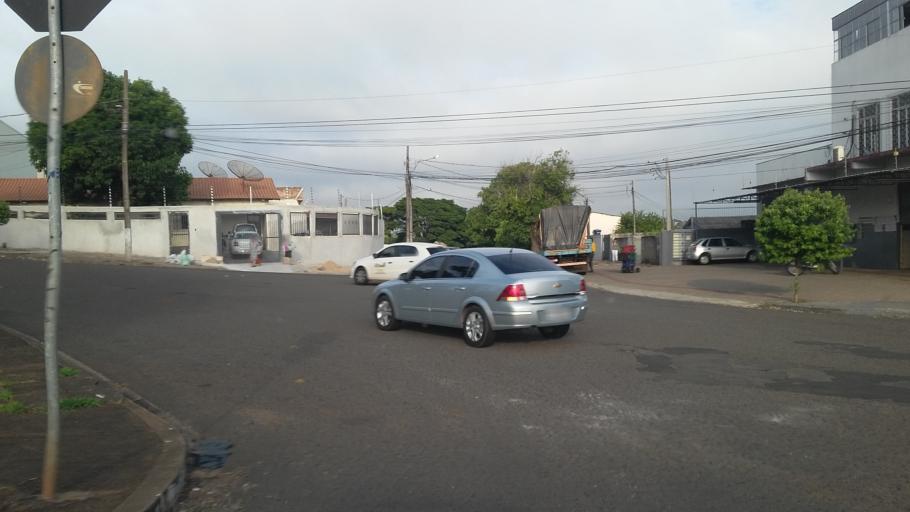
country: BR
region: Parana
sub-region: Londrina
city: Londrina
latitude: -23.2966
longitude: -51.1818
